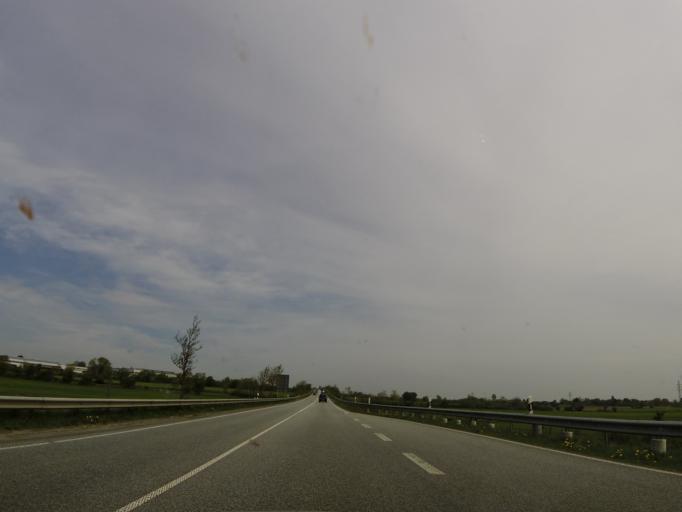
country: DE
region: Schleswig-Holstein
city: Mildstedt
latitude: 54.4749
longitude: 9.0831
